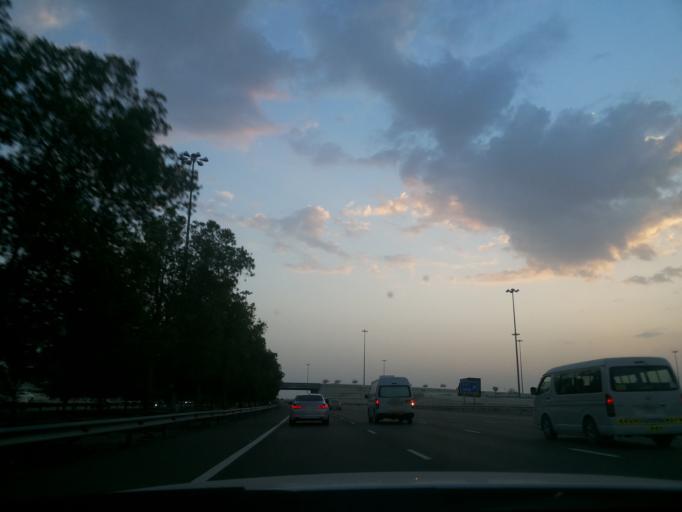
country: AE
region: Abu Dhabi
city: Abu Dhabi
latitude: 24.6229
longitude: 54.7181
